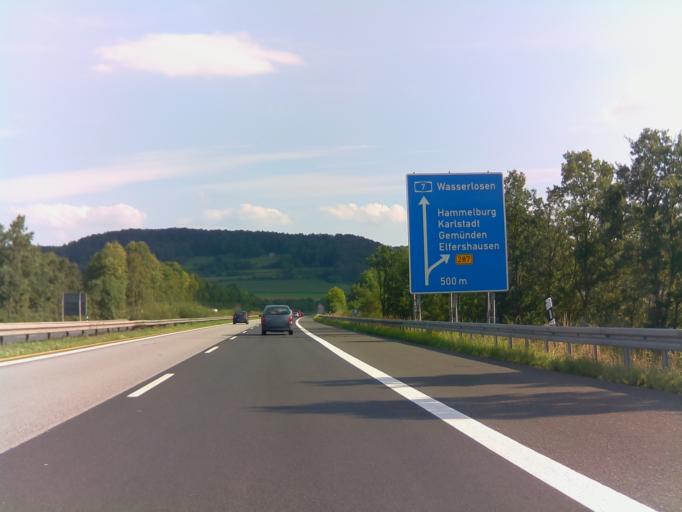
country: DE
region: Bavaria
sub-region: Regierungsbezirk Unterfranken
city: Elfershausen
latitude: 50.1330
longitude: 9.9542
